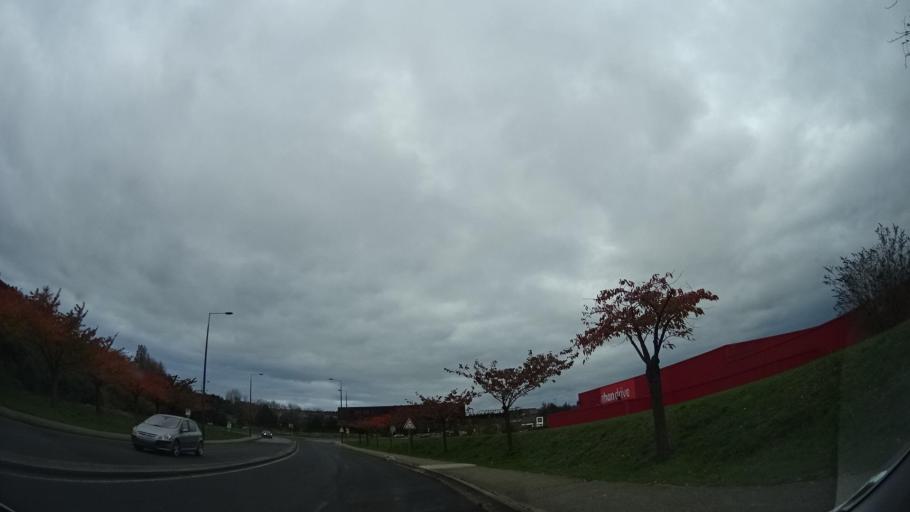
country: FR
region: Haute-Normandie
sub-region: Departement de la Seine-Maritime
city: Sainte-Adresse
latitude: 49.5248
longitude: 0.1078
